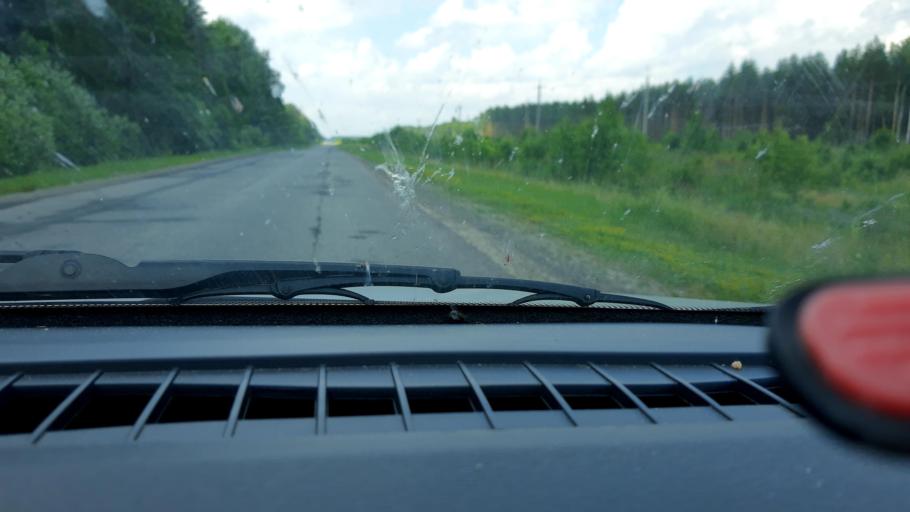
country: RU
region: Nizjnij Novgorod
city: Prudy
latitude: 57.4434
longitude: 46.0552
